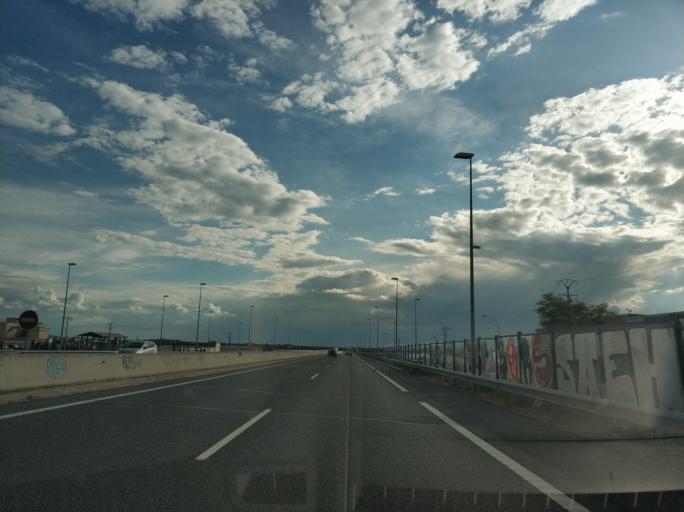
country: ES
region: Castille and Leon
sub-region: Provincia de Valladolid
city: Cisterniga
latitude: 41.6156
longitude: -4.7064
